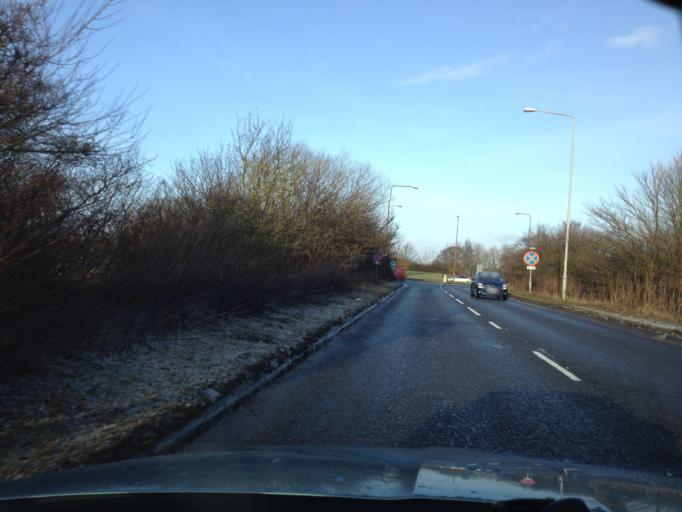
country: GB
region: Scotland
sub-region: West Lothian
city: Whitburn
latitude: 55.8792
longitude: -3.6591
